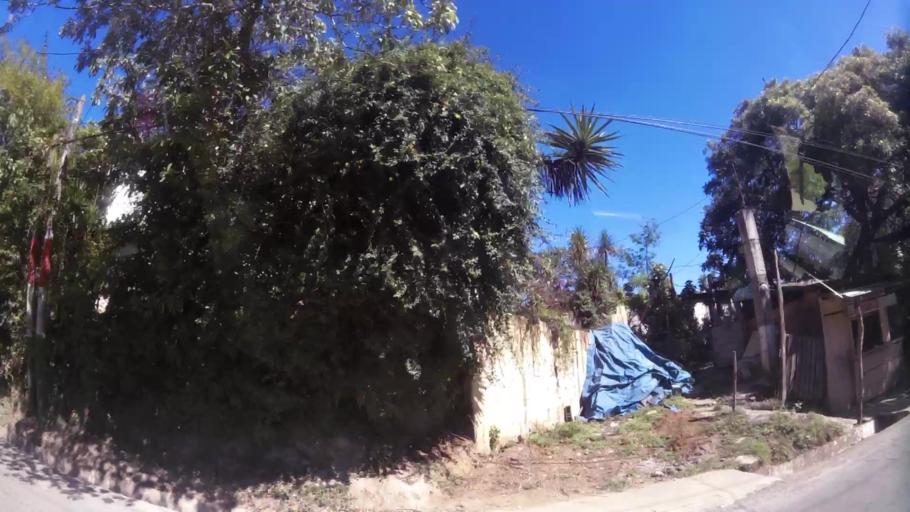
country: GT
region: Guatemala
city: San Jose Pinula
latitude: 14.5149
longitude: -90.4299
